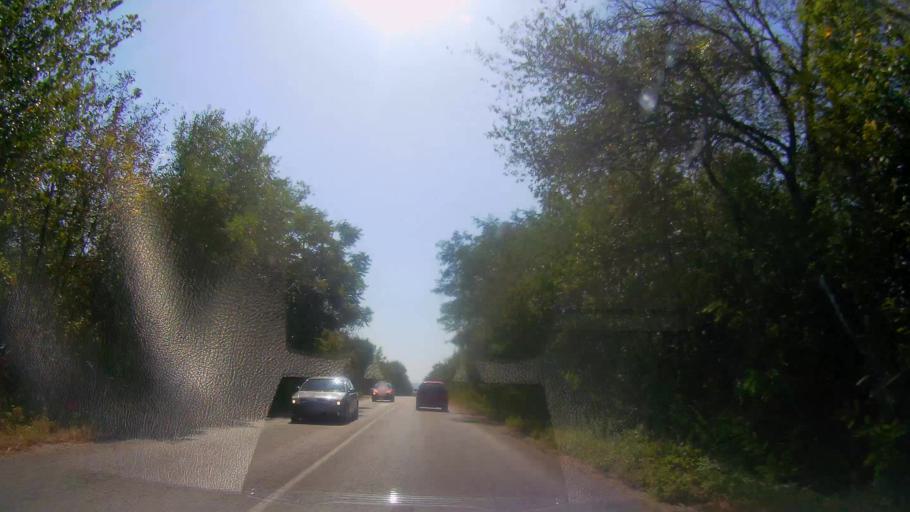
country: BG
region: Veliko Turnovo
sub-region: Obshtina Gorna Oryakhovitsa
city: Purvomaytsi
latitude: 43.2552
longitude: 25.6426
